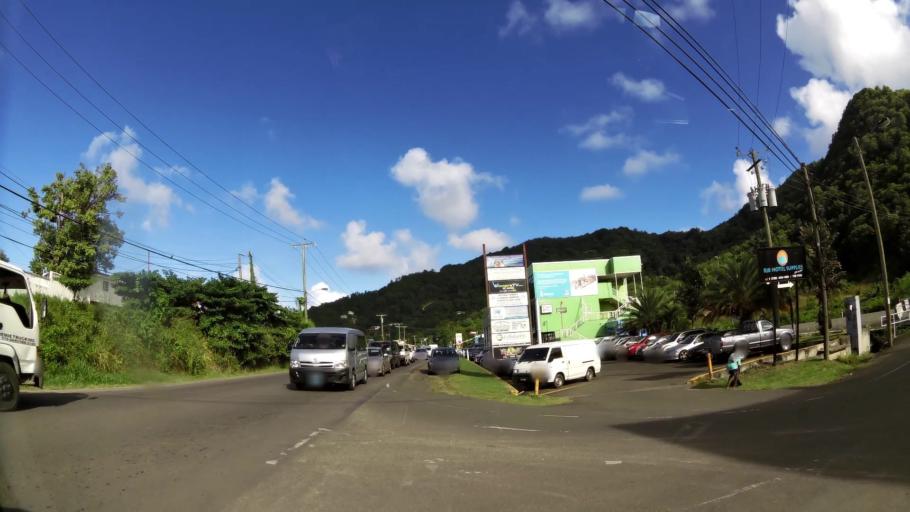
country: LC
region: Gros-Islet
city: Gros Islet
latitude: 14.0544
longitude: -60.9633
